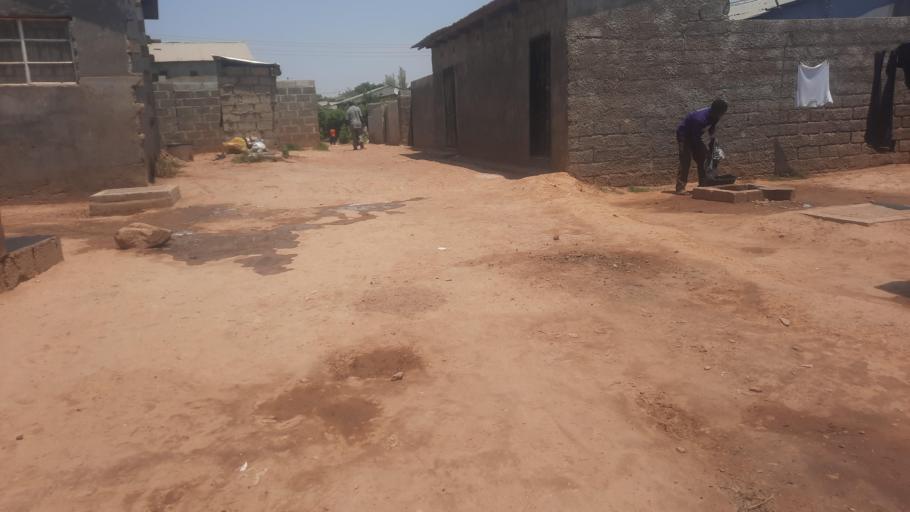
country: ZM
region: Lusaka
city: Lusaka
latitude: -15.4020
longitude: 28.3741
